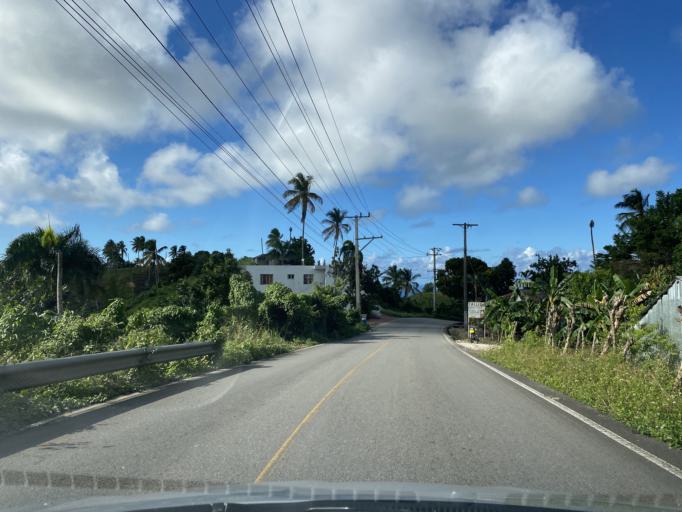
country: DO
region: Samana
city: Las Terrenas
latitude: 19.2768
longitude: -69.5531
